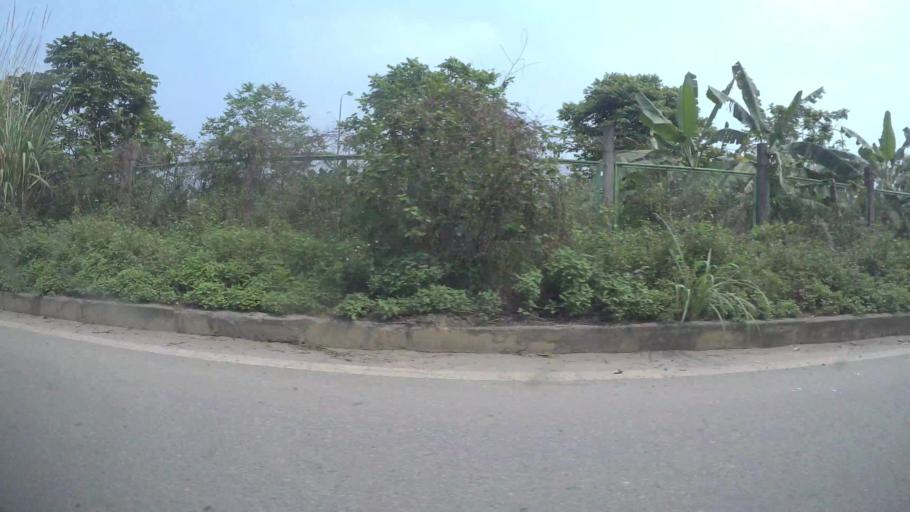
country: VN
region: Ha Noi
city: Lien Quan
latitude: 20.9899
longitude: 105.5395
